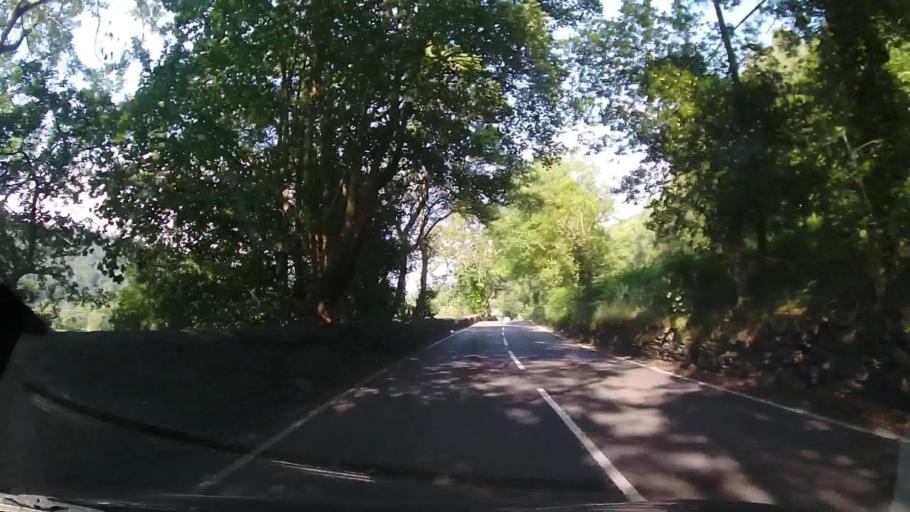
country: GB
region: Wales
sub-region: Gwynedd
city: Maentwrog
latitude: 52.9484
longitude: -3.9828
